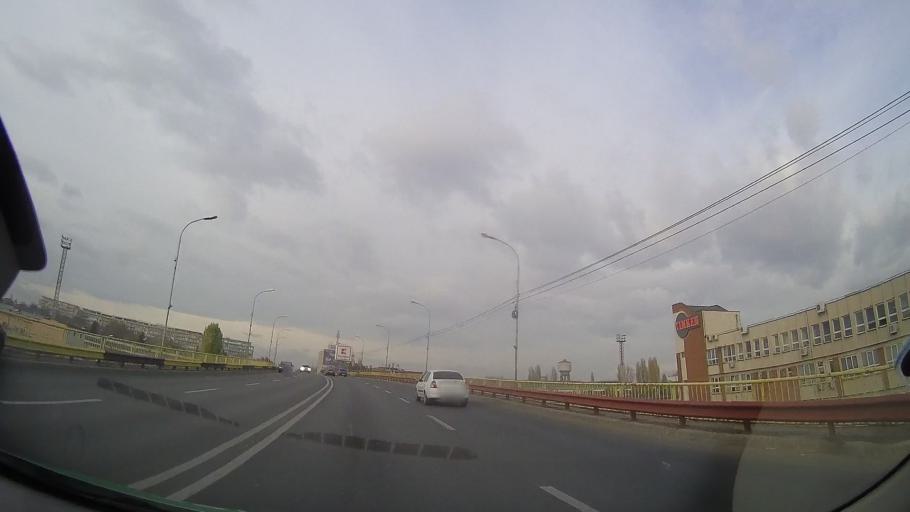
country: RO
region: Prahova
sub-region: Comuna Barcanesti
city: Tatarani
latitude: 44.9244
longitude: 26.0342
